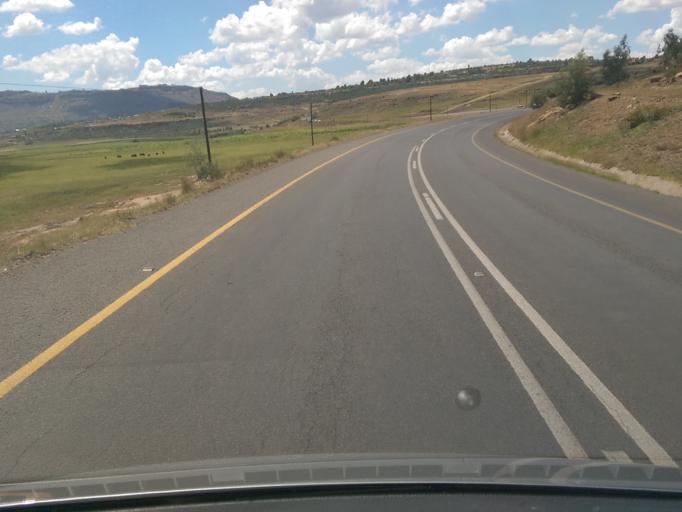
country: LS
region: Maseru
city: Maseru
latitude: -29.3914
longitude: 27.5041
